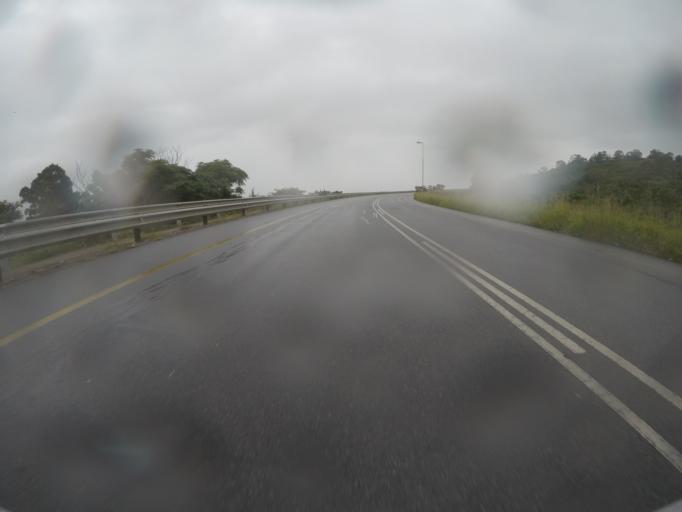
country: ZA
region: Eastern Cape
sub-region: Buffalo City Metropolitan Municipality
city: East London
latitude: -32.9571
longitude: 27.9141
